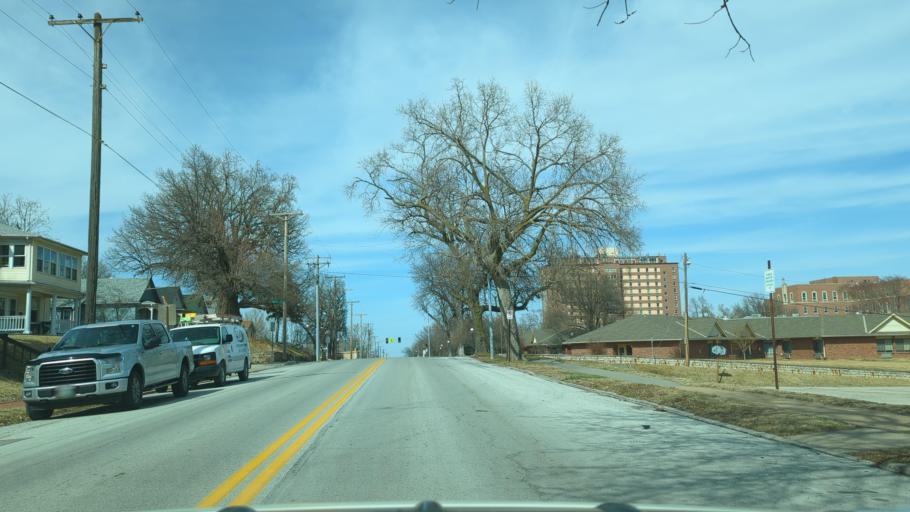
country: US
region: Nebraska
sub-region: Douglas County
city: Omaha
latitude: 41.2363
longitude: -95.9295
